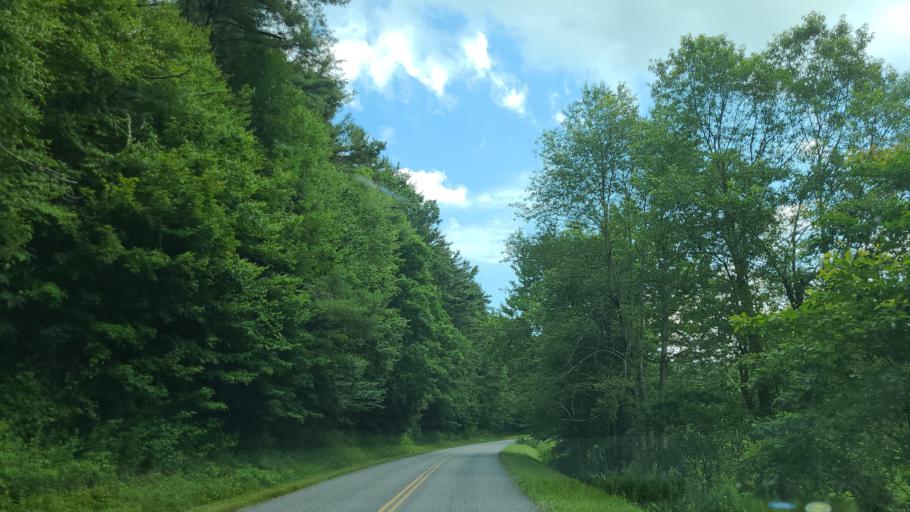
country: US
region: North Carolina
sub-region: Avery County
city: Newland
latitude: 35.9864
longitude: -81.8953
